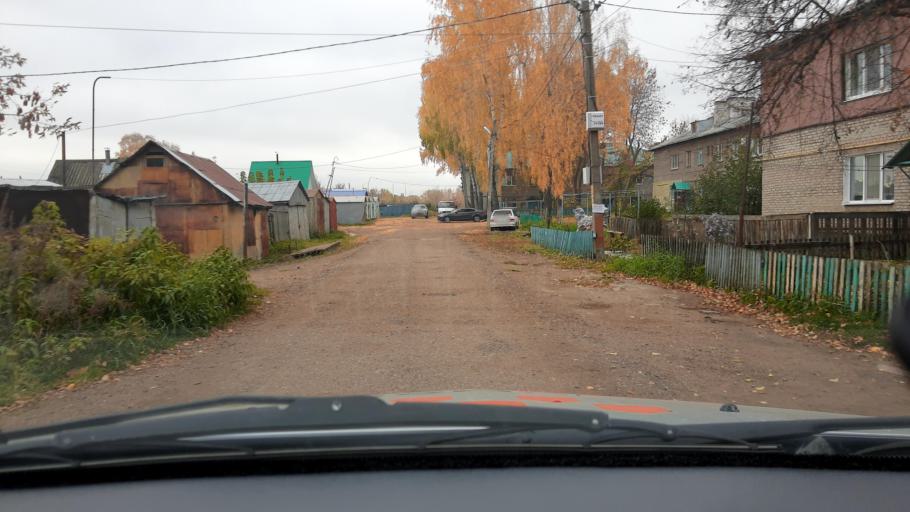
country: RU
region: Bashkortostan
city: Mikhaylovka
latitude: 54.8006
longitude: 55.8871
